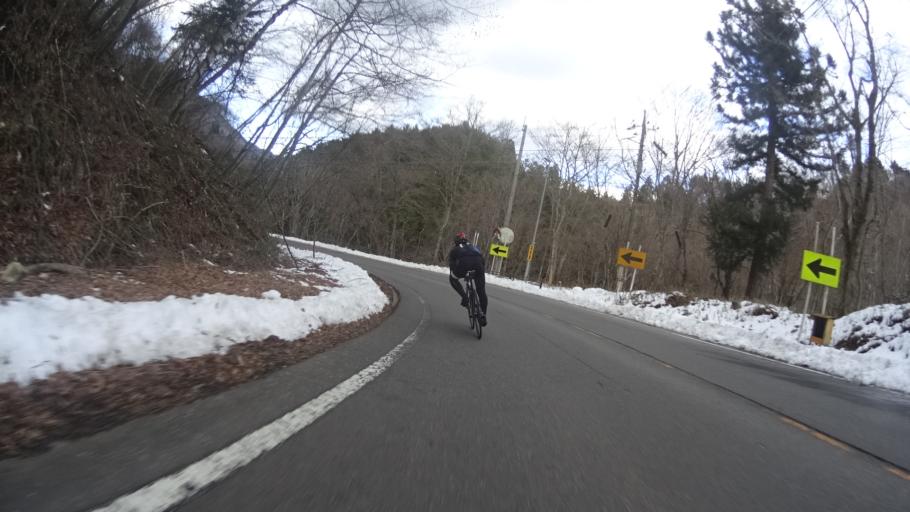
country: JP
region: Yamanashi
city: Otsuki
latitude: 35.4591
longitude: 138.9395
